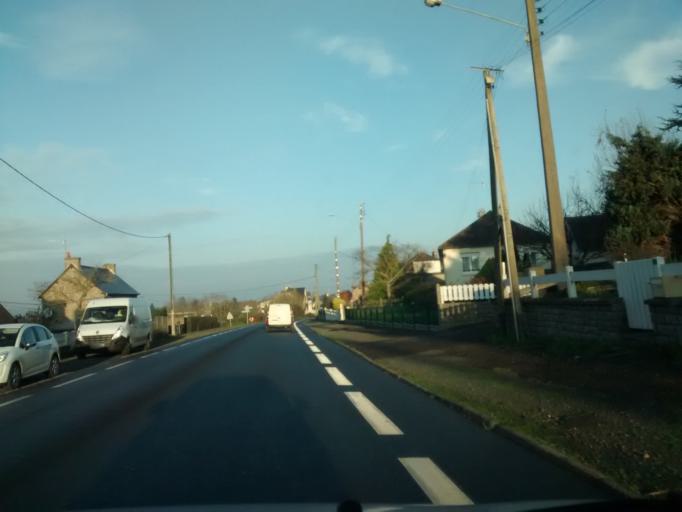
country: FR
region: Lower Normandy
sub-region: Departement de la Manche
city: Pontorson
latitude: 48.5458
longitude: -1.5009
